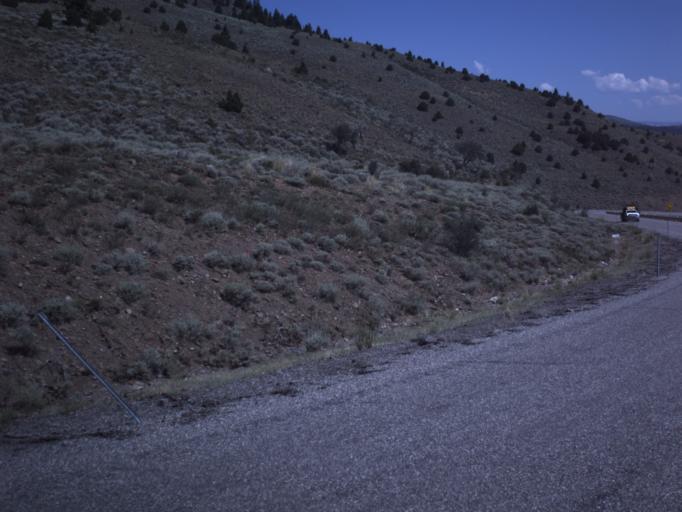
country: US
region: Utah
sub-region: Wayne County
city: Loa
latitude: 38.5975
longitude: -111.4675
